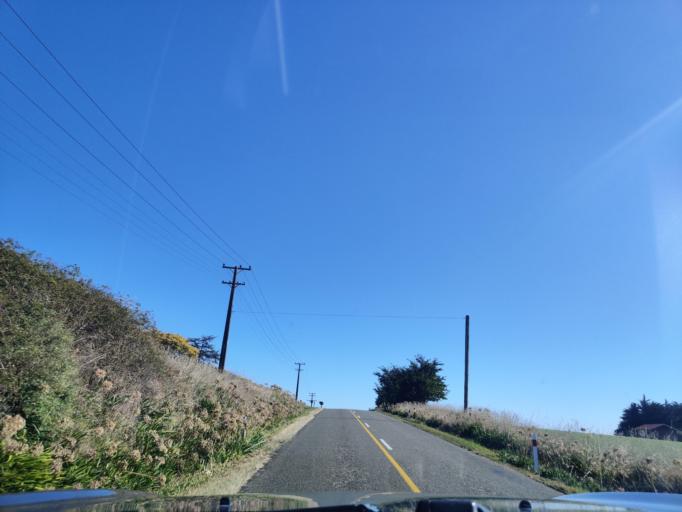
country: NZ
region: Manawatu-Wanganui
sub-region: Palmerston North City
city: Palmerston North
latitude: -40.2451
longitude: 175.6763
